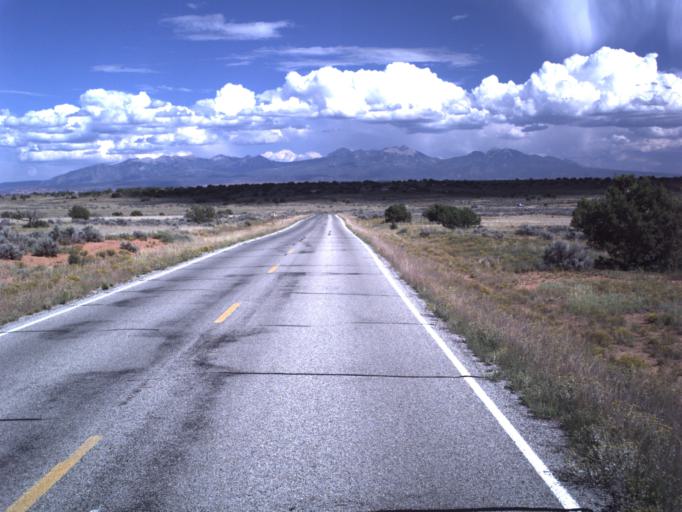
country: US
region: Utah
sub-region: Grand County
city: Moab
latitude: 38.5221
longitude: -109.7376
